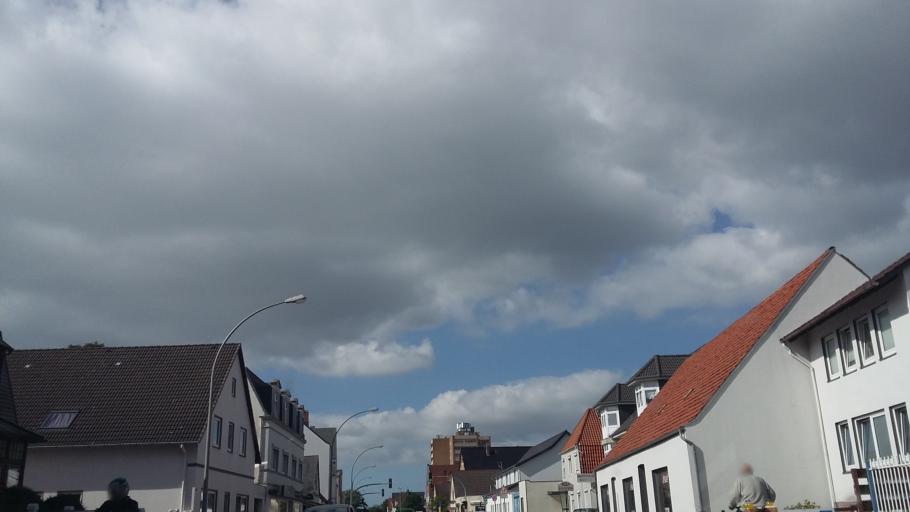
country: DE
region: Bremen
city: Bremerhaven
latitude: 53.5028
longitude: 8.6001
